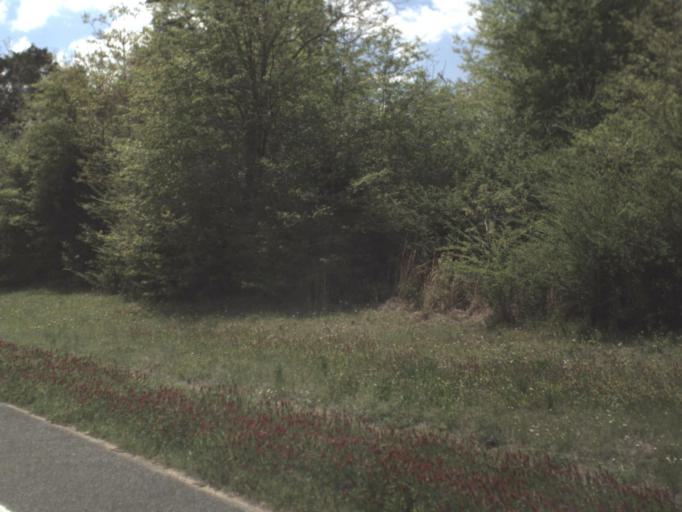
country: US
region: Florida
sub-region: Okaloosa County
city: Crestview
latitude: 30.8844
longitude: -86.6635
